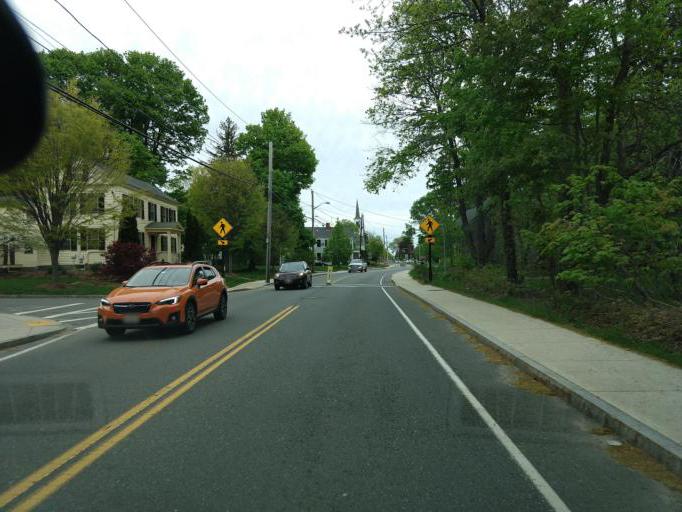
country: US
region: Massachusetts
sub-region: Middlesex County
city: Billerica
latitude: 42.5557
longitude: -71.2696
